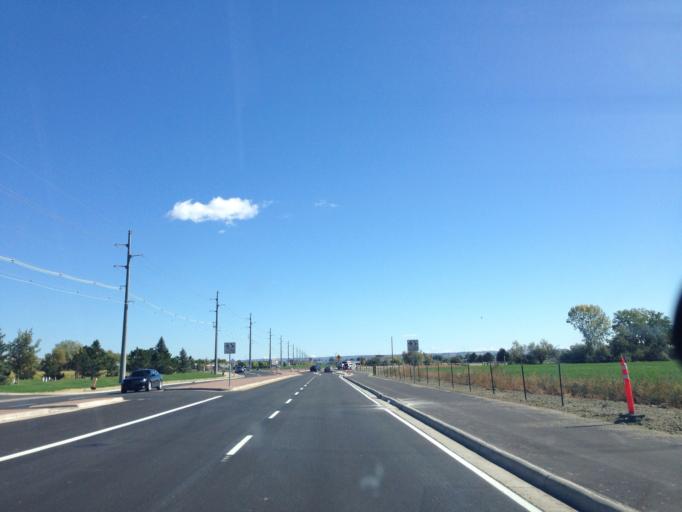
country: US
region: Montana
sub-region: Yellowstone County
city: Billings
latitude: 45.7840
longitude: -108.6080
